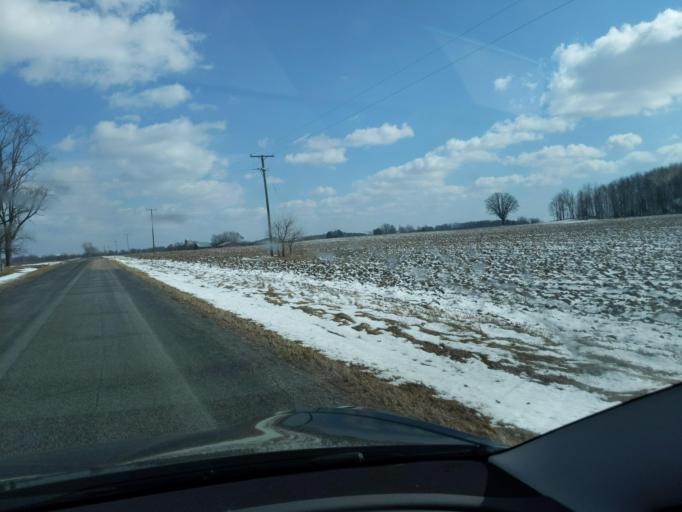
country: US
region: Michigan
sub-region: Ingham County
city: Webberville
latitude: 42.6150
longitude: -84.2043
